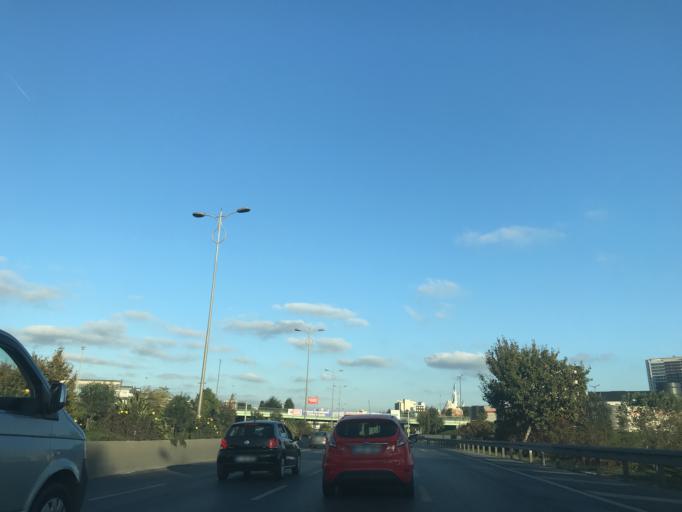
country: TR
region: Istanbul
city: Esenler
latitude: 41.0459
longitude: 28.8823
